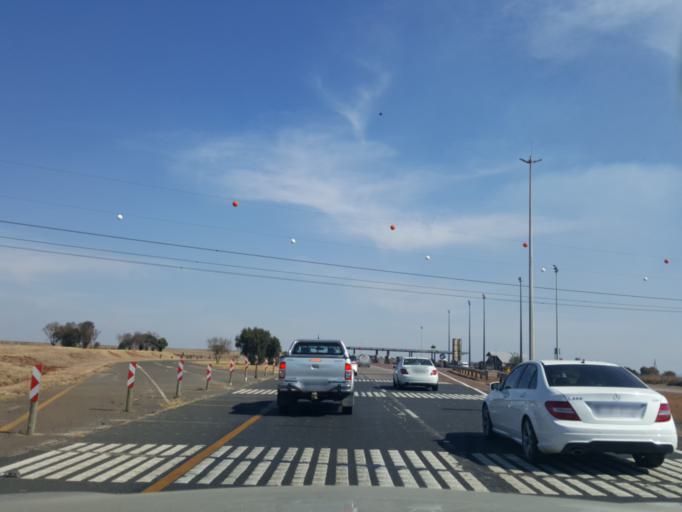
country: ZA
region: Mpumalanga
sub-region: Nkangala District Municipality
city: Middelburg
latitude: -25.8644
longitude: 29.3669
